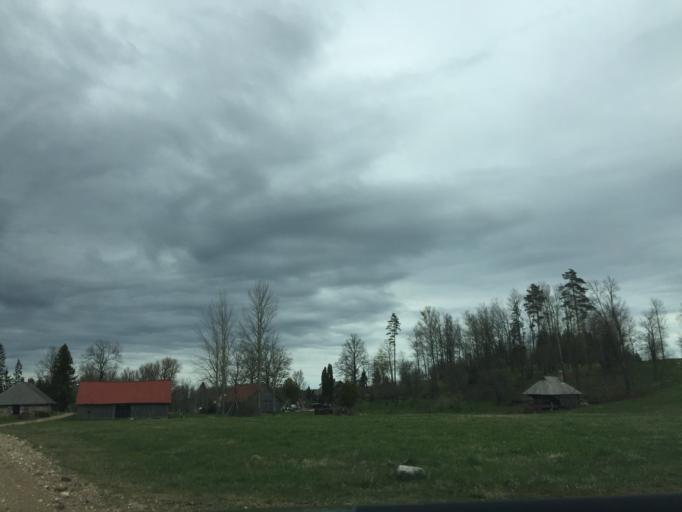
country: LV
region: Jaunpiebalga
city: Jaunpiebalga
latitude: 57.1477
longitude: 25.9295
